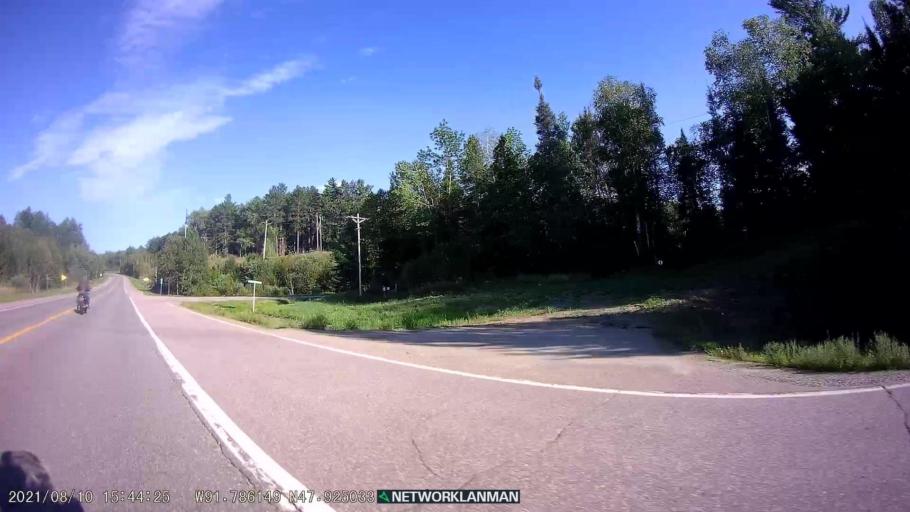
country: US
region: Minnesota
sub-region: Saint Louis County
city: Ely
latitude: 47.9250
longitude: -91.7858
